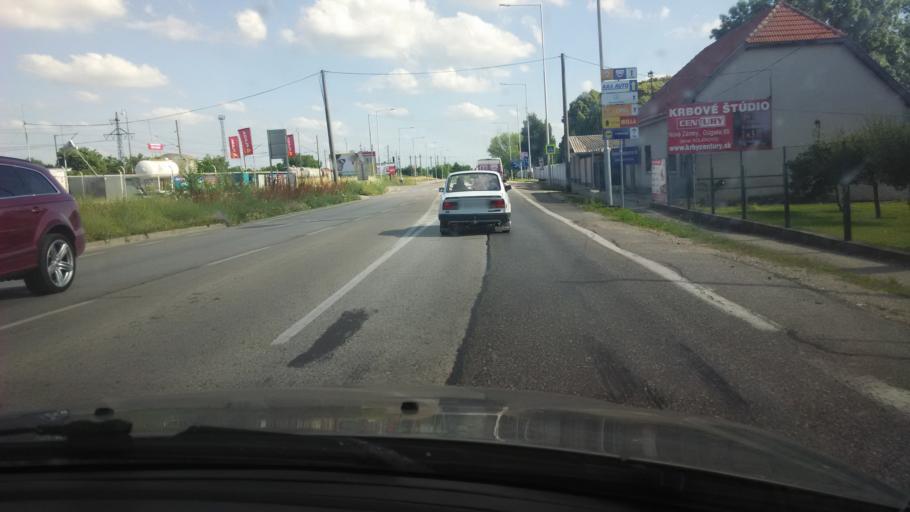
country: SK
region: Nitriansky
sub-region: Okres Nove Zamky
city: Nove Zamky
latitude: 48.0088
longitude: 18.1560
